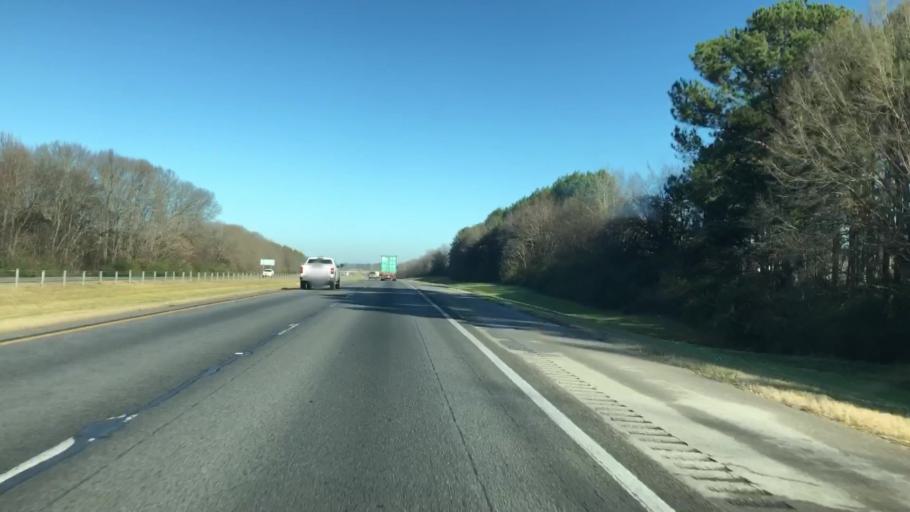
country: US
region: Alabama
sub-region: Limestone County
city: Athens
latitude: 34.7996
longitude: -86.9387
